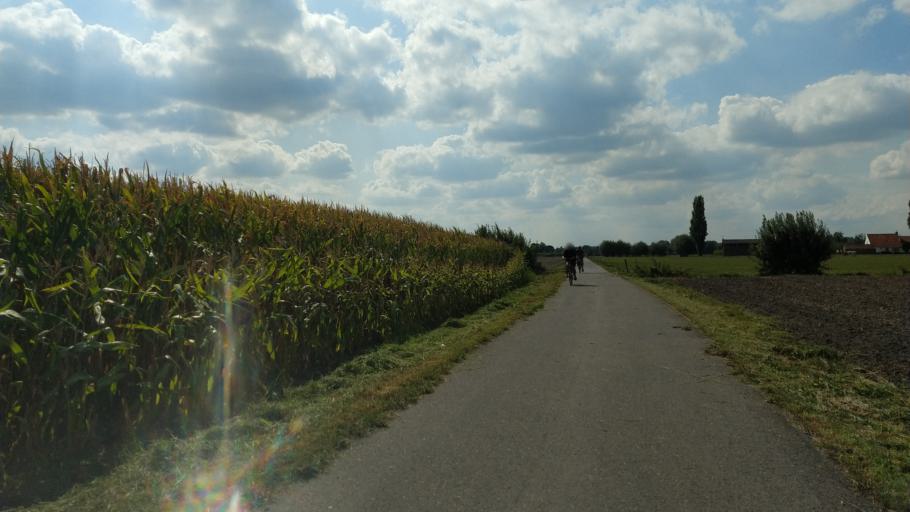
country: BE
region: Flanders
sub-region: Provincie Oost-Vlaanderen
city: Assenede
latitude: 51.2461
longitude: 3.6976
